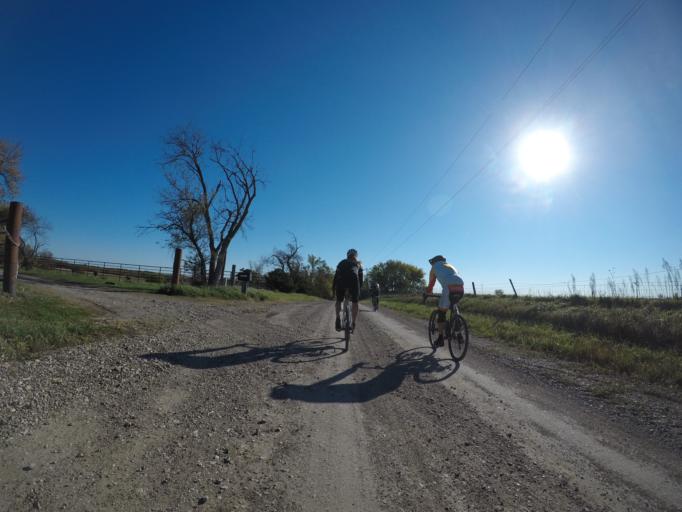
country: US
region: Kansas
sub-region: Morris County
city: Council Grove
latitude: 38.8260
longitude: -96.4681
